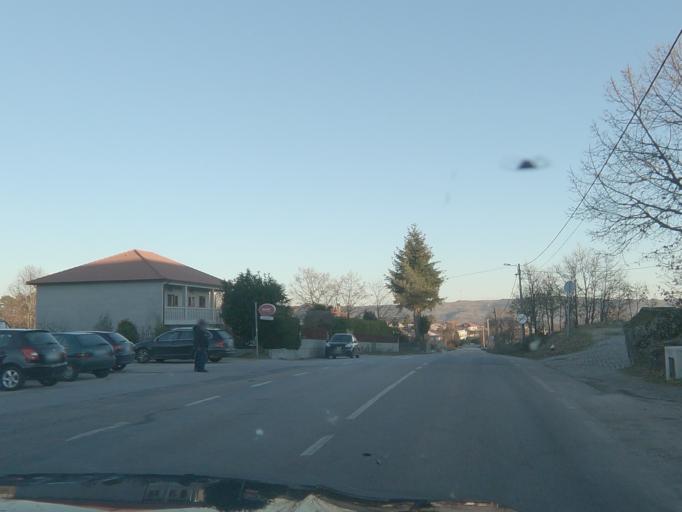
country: PT
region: Vila Real
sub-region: Vila Pouca de Aguiar
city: Vila Pouca de Aguiar
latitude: 41.5012
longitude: -7.6880
